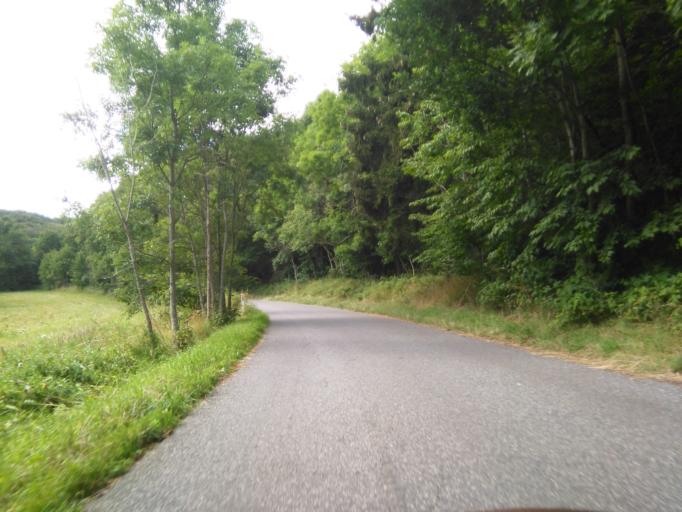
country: DK
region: Central Jutland
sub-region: Skanderborg Kommune
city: Horning
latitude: 56.1075
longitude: 10.0160
